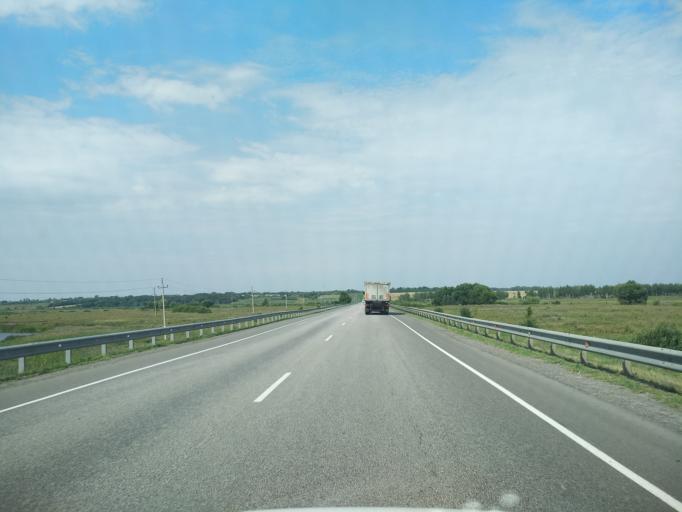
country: RU
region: Voronezj
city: Orlovo
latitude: 51.6756
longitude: 39.7426
